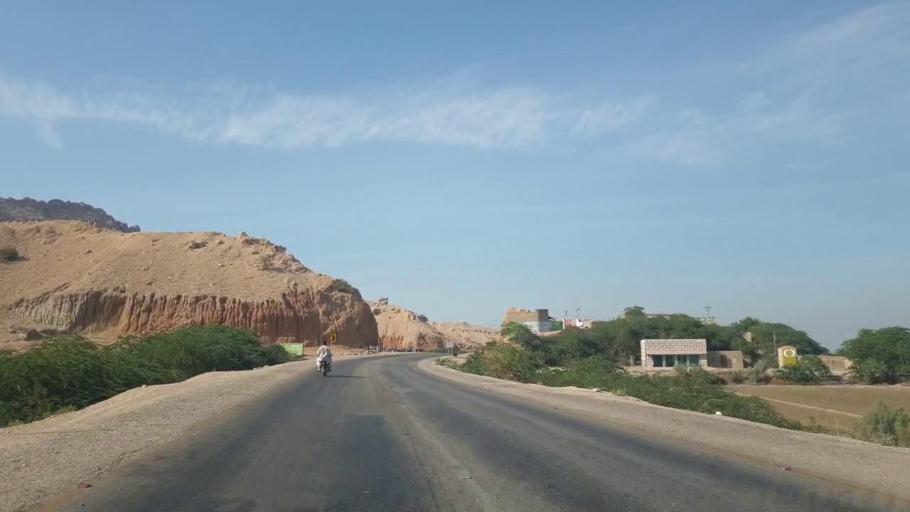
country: PK
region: Sindh
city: Sehwan
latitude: 26.3153
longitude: 67.8903
